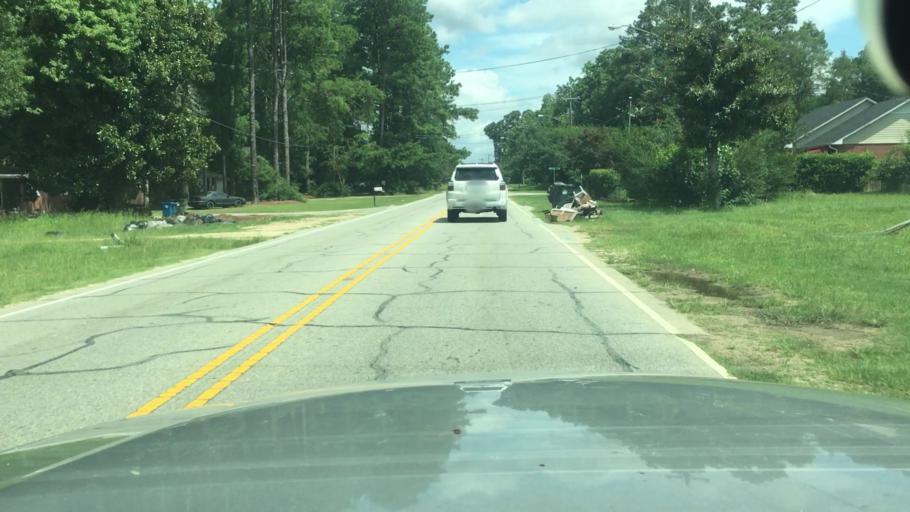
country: US
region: North Carolina
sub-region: Hoke County
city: Rockfish
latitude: 35.0352
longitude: -78.9974
